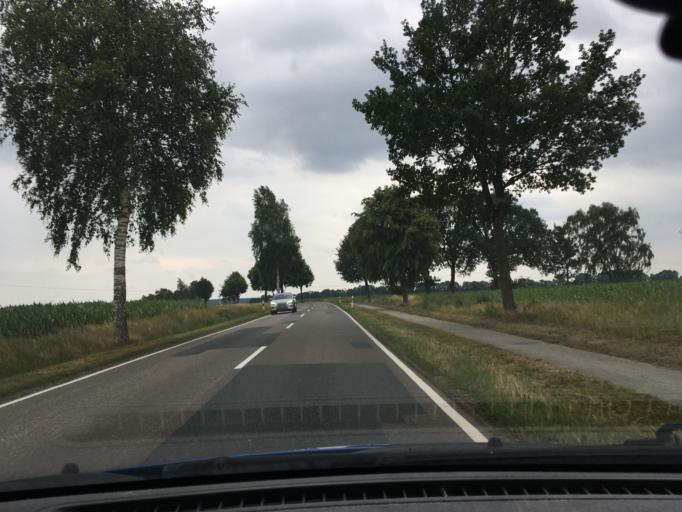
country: DE
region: Lower Saxony
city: Kakenstorf
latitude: 53.3248
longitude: 9.7779
